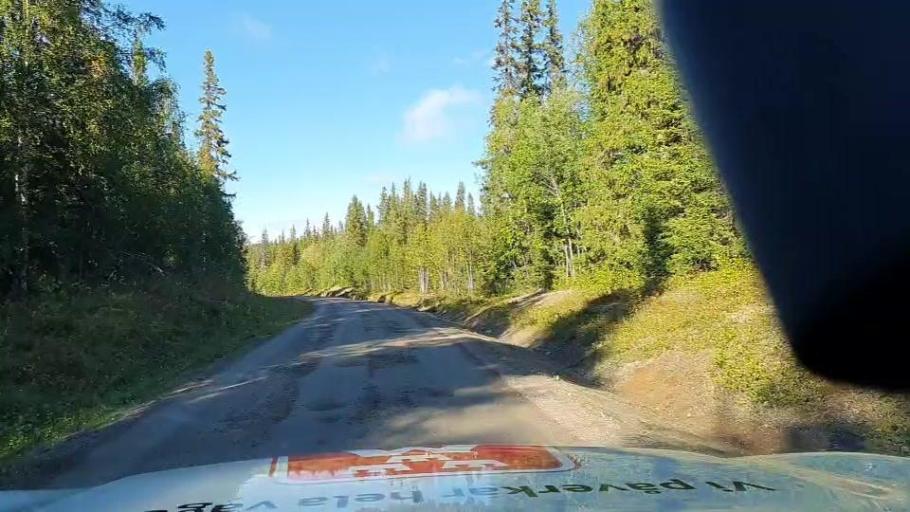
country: SE
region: Jaemtland
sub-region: Stroemsunds Kommun
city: Stroemsund
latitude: 64.5581
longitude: 15.0943
